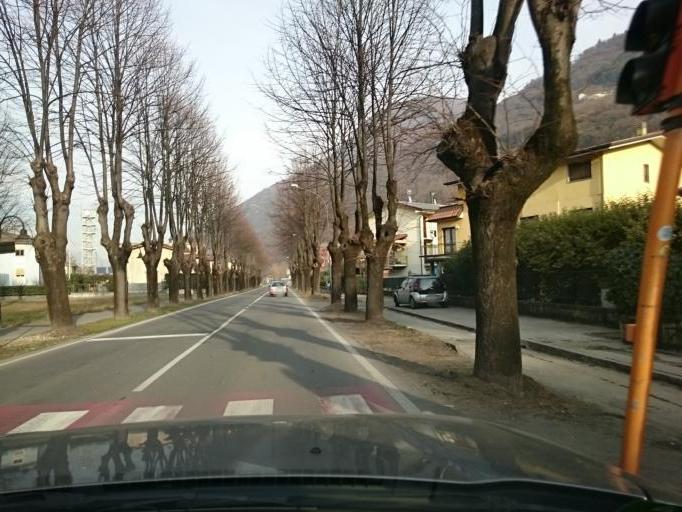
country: IT
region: Lombardy
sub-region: Provincia di Brescia
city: Pisogne
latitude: 45.8096
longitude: 10.1099
